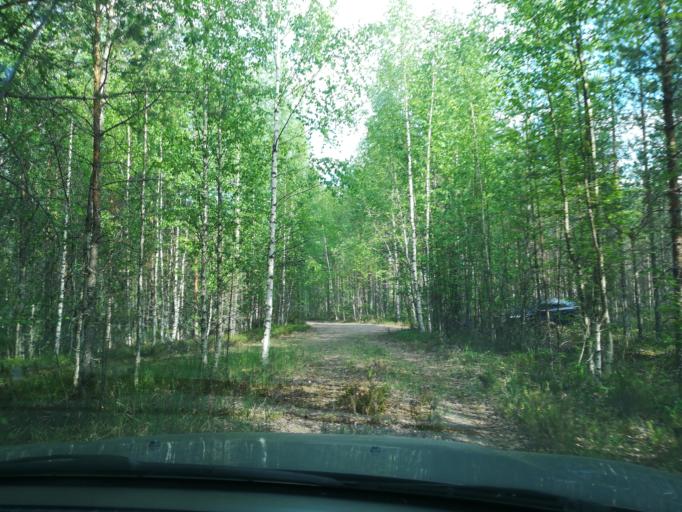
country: FI
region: Southern Savonia
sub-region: Savonlinna
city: Savonlinna
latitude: 61.6438
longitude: 28.7144
